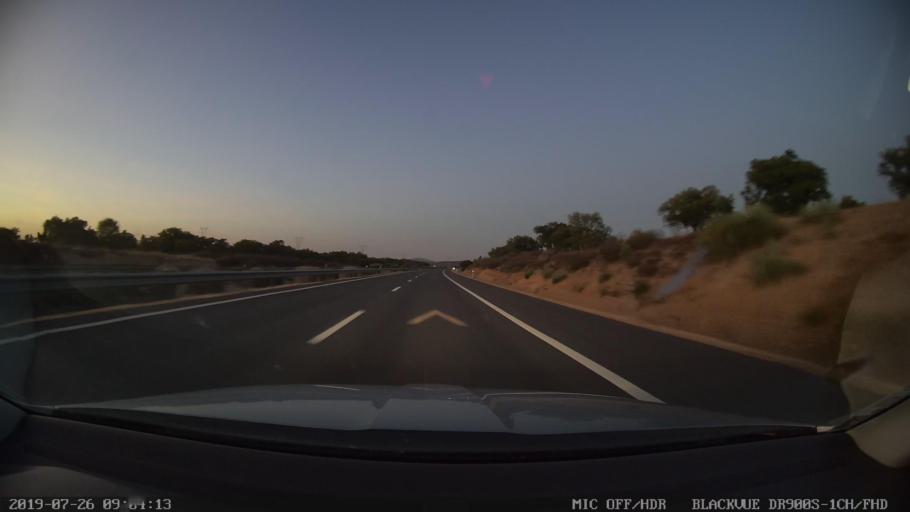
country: PT
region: Evora
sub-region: Evora
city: Evora
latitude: 38.7073
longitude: -7.7966
